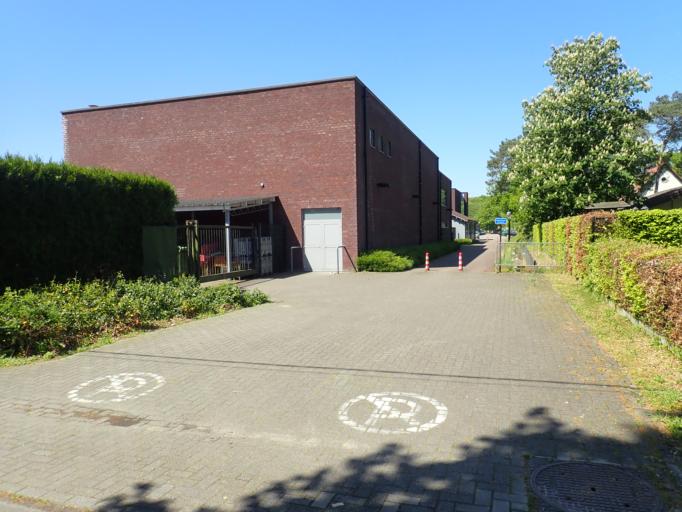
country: BE
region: Flanders
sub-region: Provincie Antwerpen
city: Zandhoven
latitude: 51.2335
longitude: 4.6894
